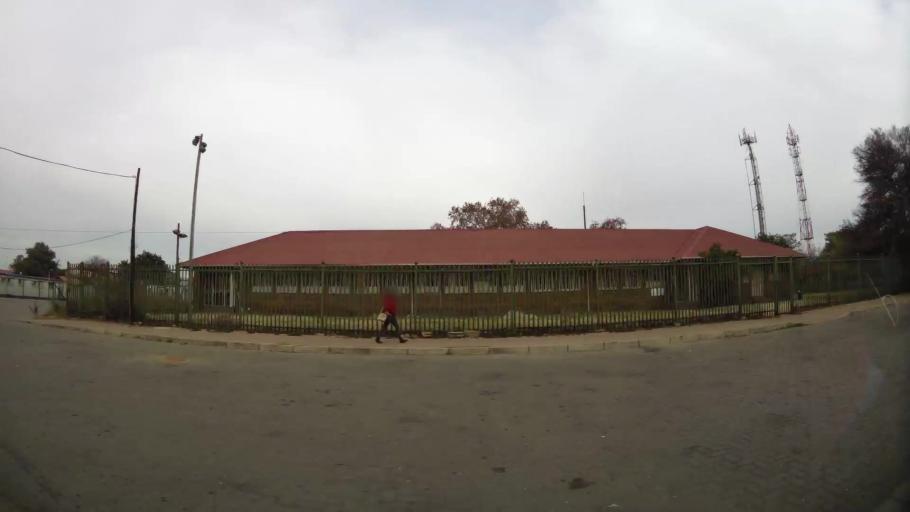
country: ZA
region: Gauteng
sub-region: City of Tshwane Metropolitan Municipality
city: Pretoria
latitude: -25.7137
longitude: 28.3472
